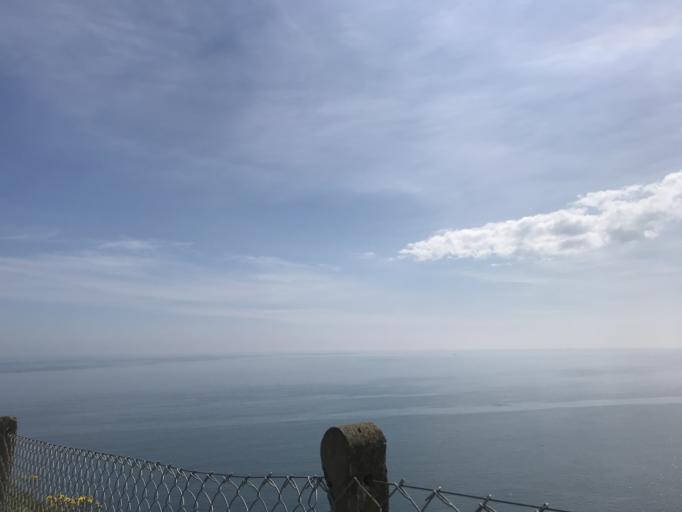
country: IE
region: Leinster
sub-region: Wicklow
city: Bray
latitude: 53.1873
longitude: -6.0775
